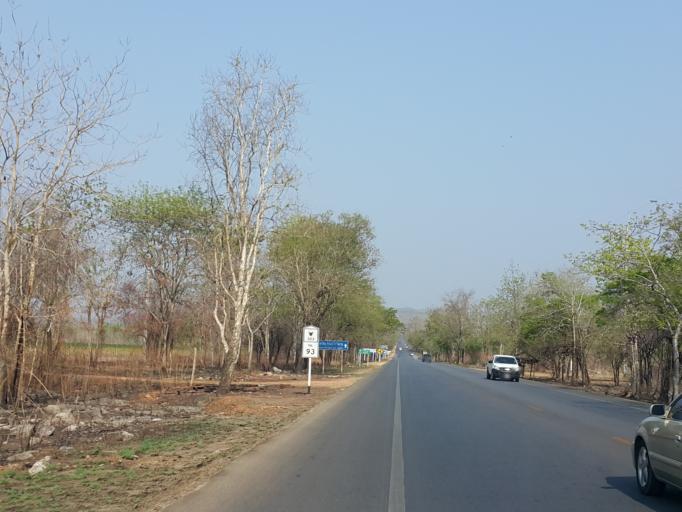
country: TH
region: Kanchanaburi
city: Sai Yok
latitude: 14.0956
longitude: 99.2546
